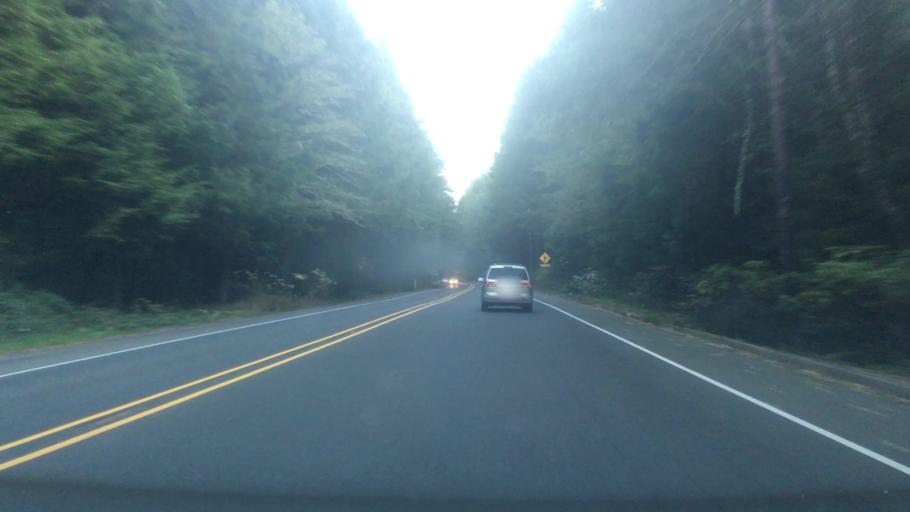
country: US
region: Oregon
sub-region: Clatsop County
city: Cannon Beach
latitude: 45.7848
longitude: -123.9581
